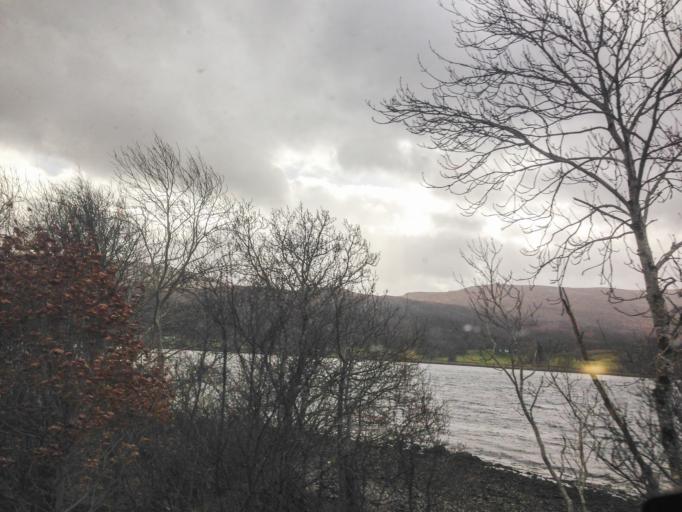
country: GB
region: Scotland
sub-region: Highland
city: Fort William
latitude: 56.8515
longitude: -5.1720
